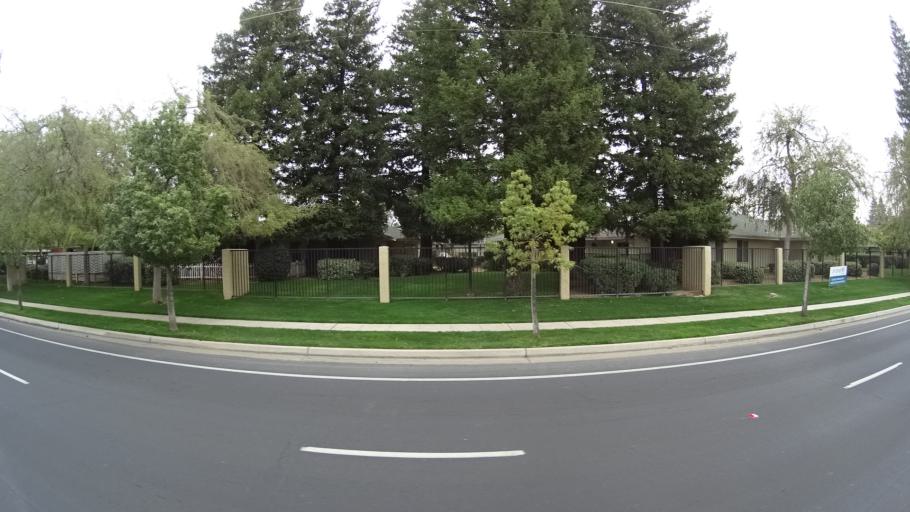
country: US
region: California
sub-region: Fresno County
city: Clovis
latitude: 36.8418
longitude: -119.7657
